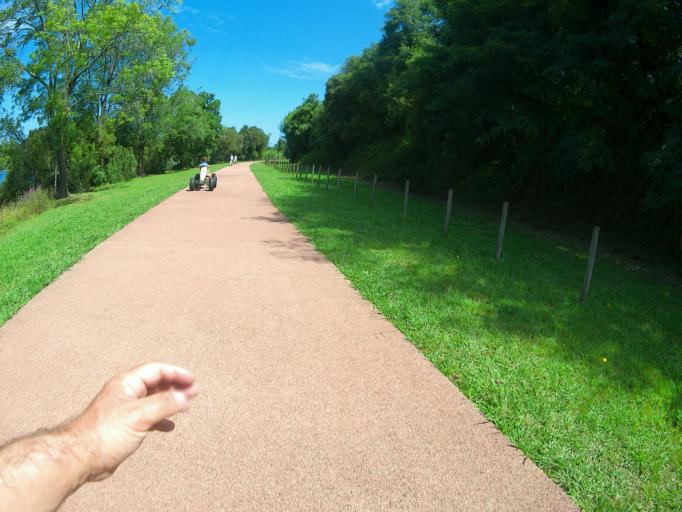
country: PT
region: Viana do Castelo
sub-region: Vila Nova de Cerveira
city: Vila Nova de Cerveira
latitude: 41.9326
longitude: -8.7529
